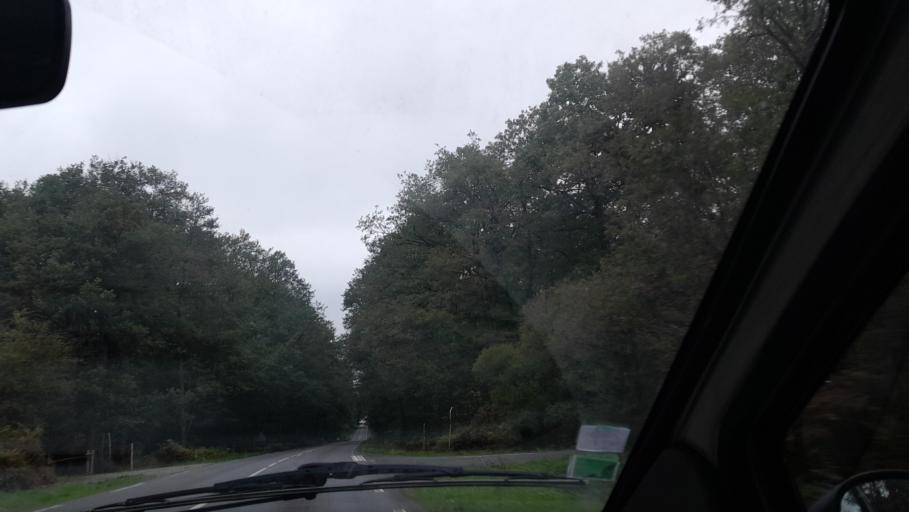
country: FR
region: Pays de la Loire
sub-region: Departement de Maine-et-Loire
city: Pouance
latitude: 47.6870
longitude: -1.1852
